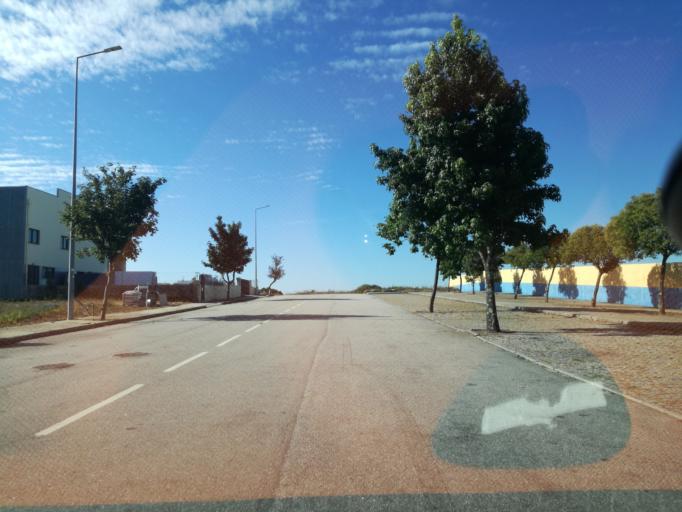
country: PT
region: Porto
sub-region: Pacos de Ferreira
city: Seroa
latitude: 41.2618
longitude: -8.4495
